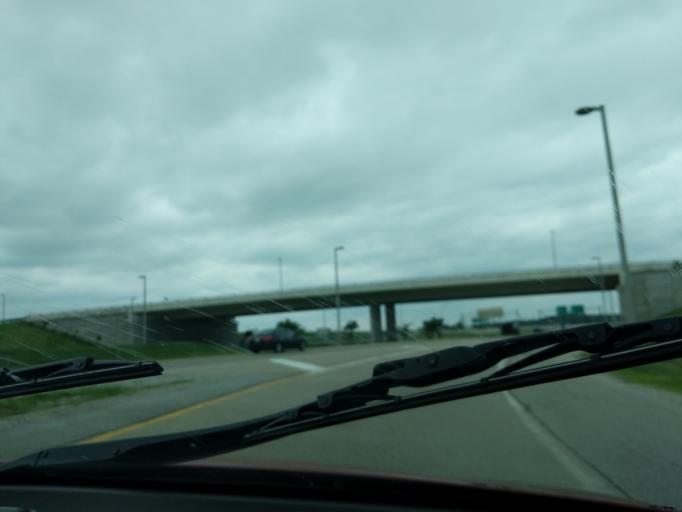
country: US
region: Indiana
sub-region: Hendricks County
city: Plainfield
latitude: 39.7004
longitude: -86.3170
